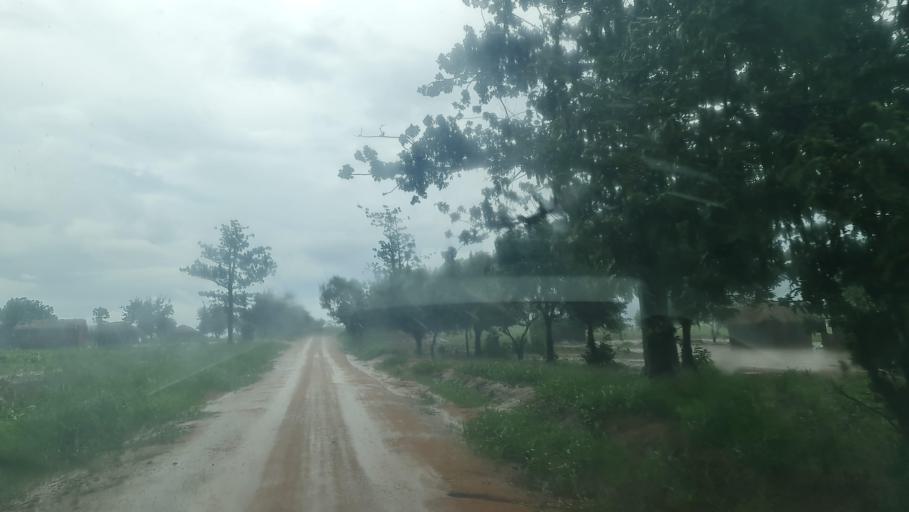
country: MW
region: Southern Region
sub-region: Nsanje District
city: Nsanje
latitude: -17.4028
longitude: 35.5948
